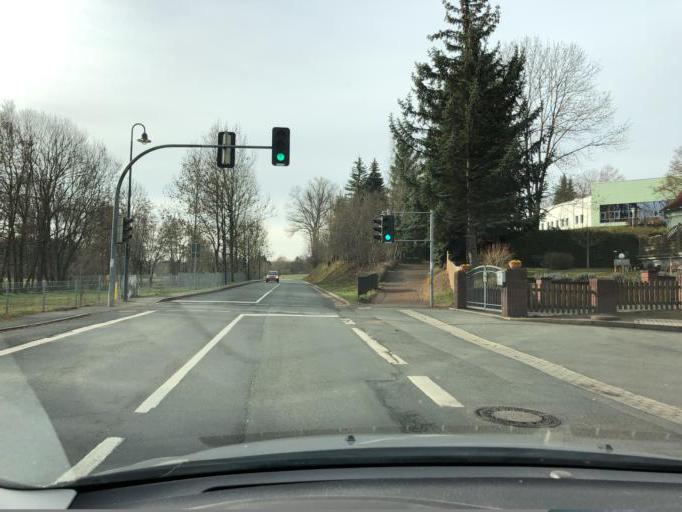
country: DE
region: Saxony-Anhalt
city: Bad Bibra
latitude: 51.2025
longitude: 11.5800
